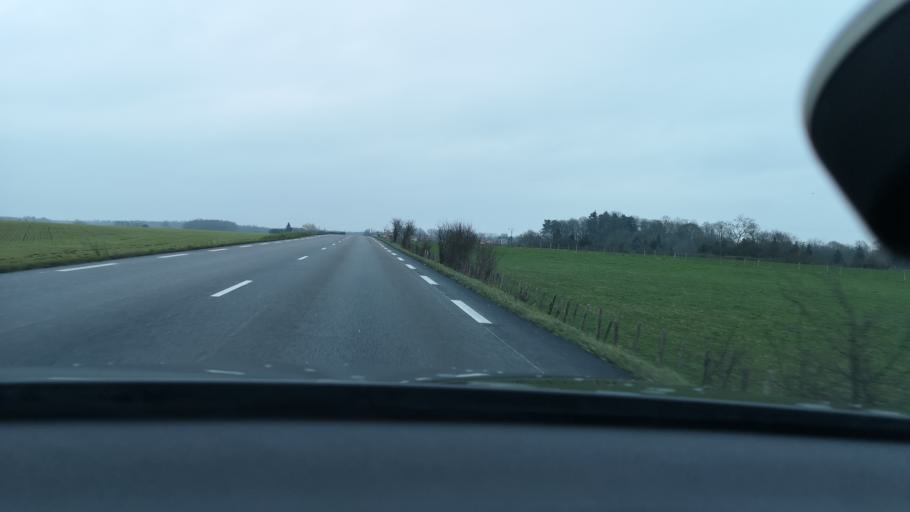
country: FR
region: Bourgogne
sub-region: Departement de la Cote-d'Or
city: Seurre
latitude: 46.9560
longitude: 5.1640
